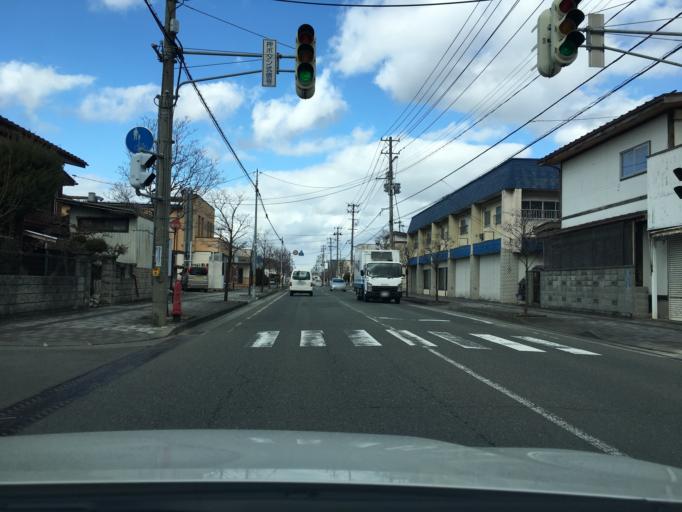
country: JP
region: Yamagata
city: Yamagata-shi
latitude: 38.2558
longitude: 140.3219
